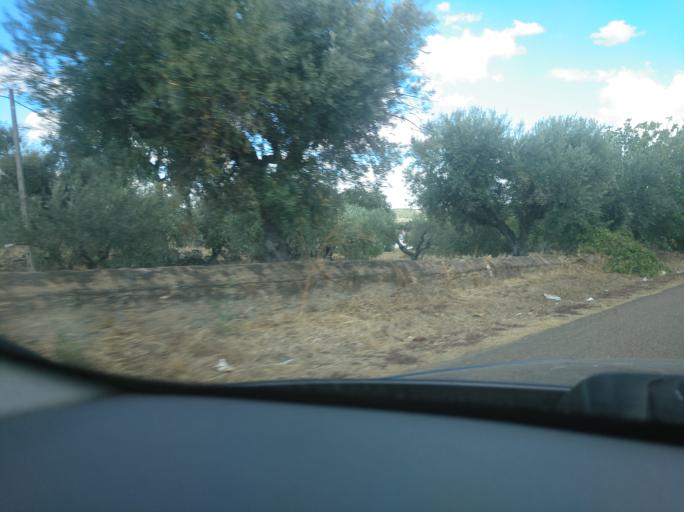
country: ES
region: Extremadura
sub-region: Provincia de Badajoz
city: La Codosera
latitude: 39.1543
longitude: -7.1670
